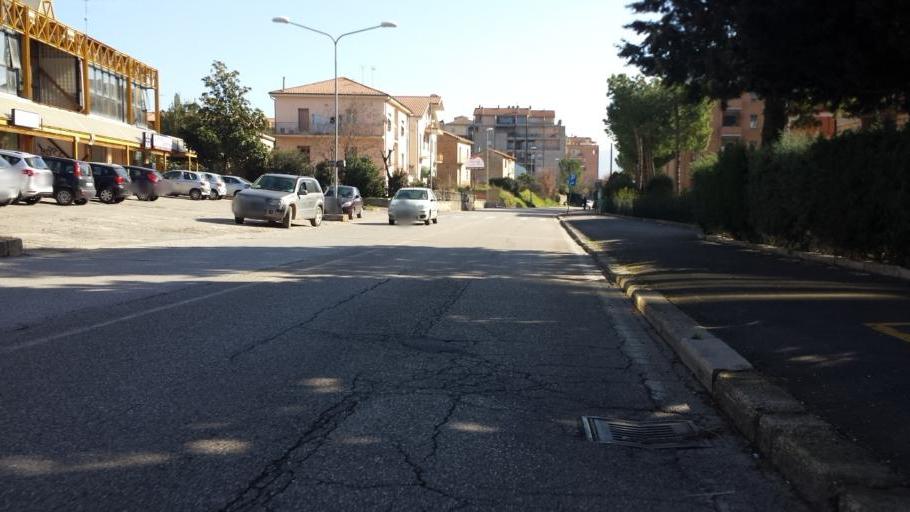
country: IT
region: Umbria
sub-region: Provincia di Terni
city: Terni
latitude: 42.5871
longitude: 12.6086
